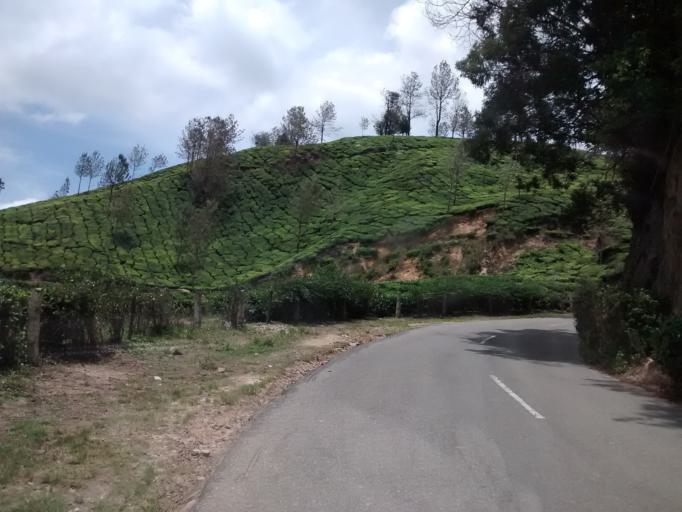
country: IN
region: Tamil Nadu
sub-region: Theni
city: Bodinayakkanur
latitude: 10.1301
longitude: 77.2299
